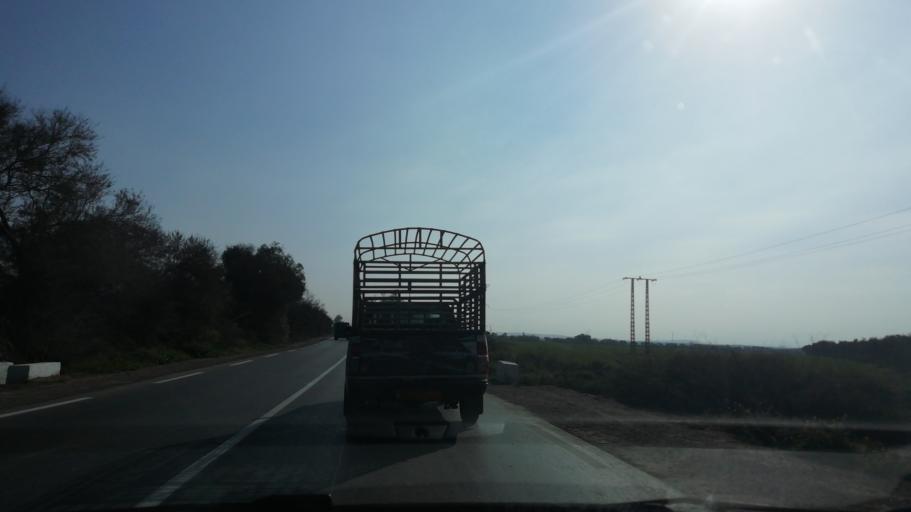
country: DZ
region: Mostaganem
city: Mostaganem
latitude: 35.7425
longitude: -0.0098
